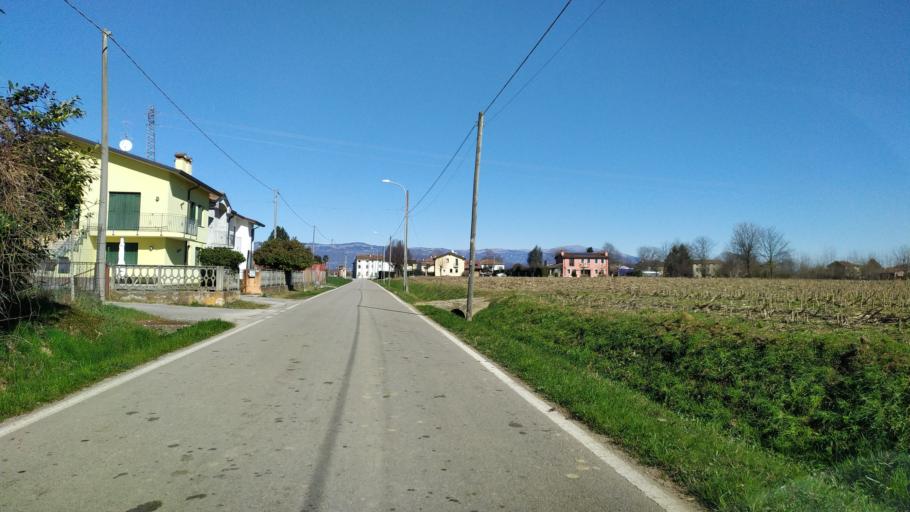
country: IT
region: Veneto
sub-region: Provincia di Vicenza
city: Monticello Conte Otto
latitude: 45.6115
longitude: 11.5743
